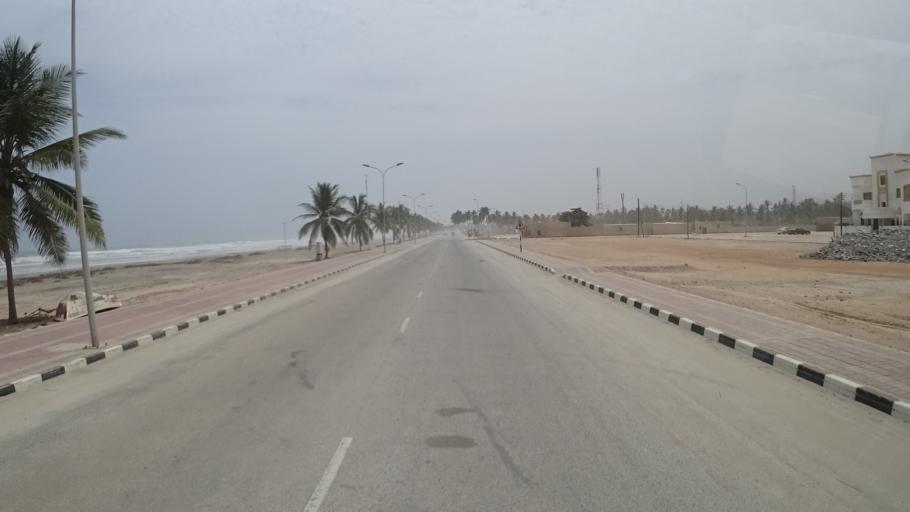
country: OM
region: Zufar
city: Salalah
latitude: 17.0343
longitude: 54.3964
